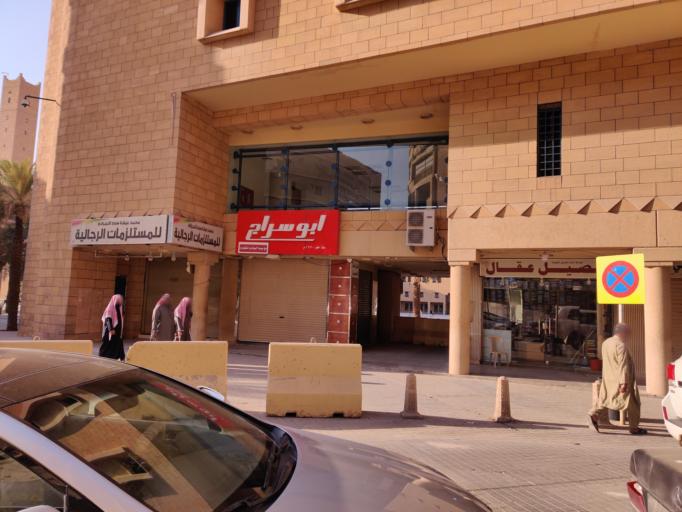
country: SA
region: Ar Riyad
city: Riyadh
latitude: 24.6303
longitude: 46.7122
